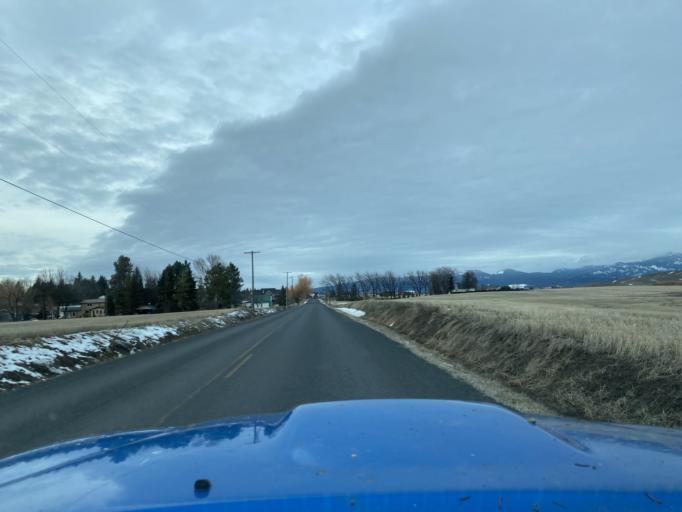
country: US
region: Idaho
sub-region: Latah County
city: Moscow
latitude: 46.7139
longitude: -116.9591
